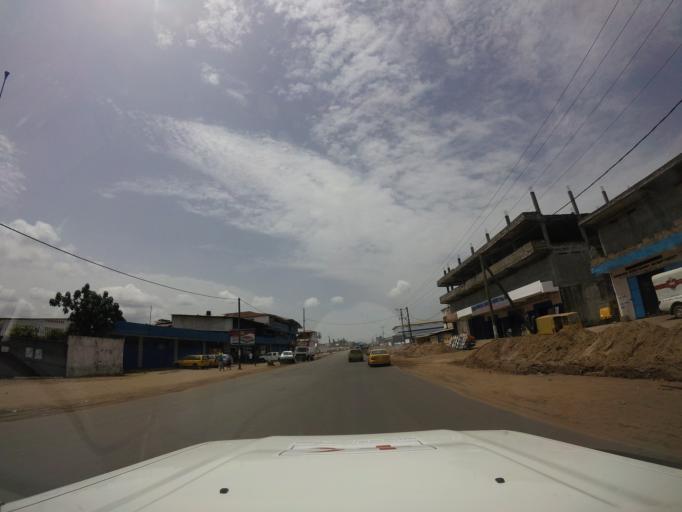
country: LR
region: Montserrado
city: Monrovia
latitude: 6.3581
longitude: -10.7864
